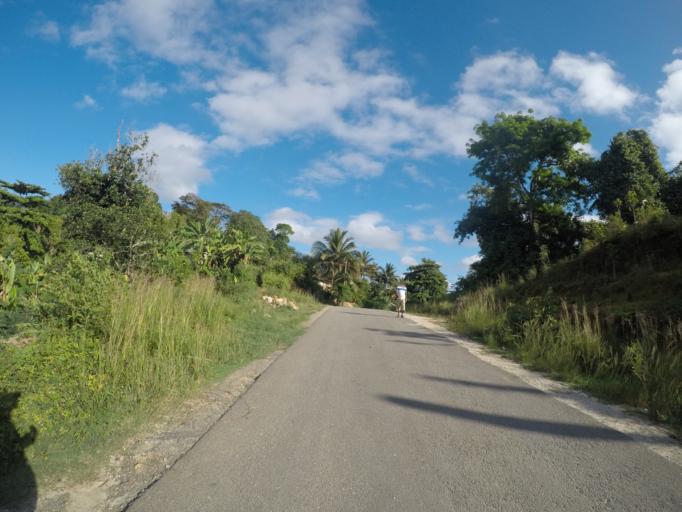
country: TZ
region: Pemba South
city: Mtambile
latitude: -5.3574
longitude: 39.7094
